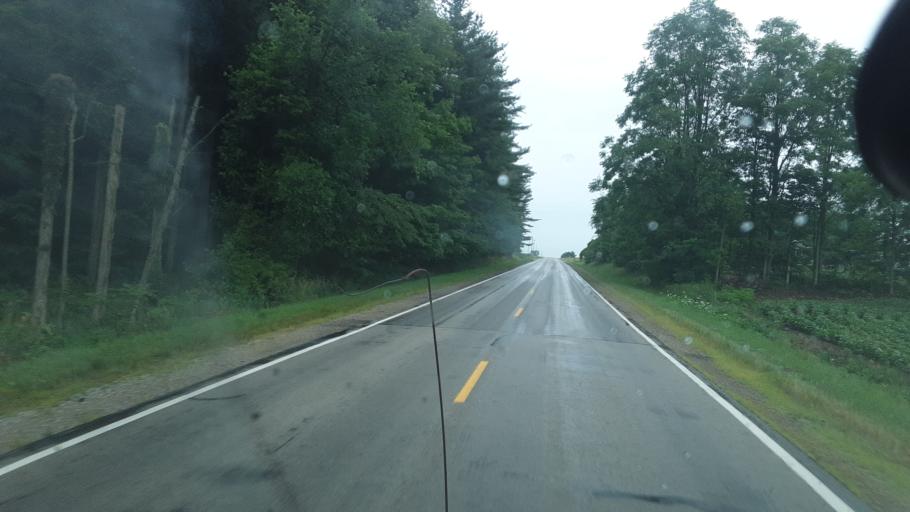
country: US
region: Indiana
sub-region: Steuben County
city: Hamilton
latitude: 41.5586
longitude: -84.8498
